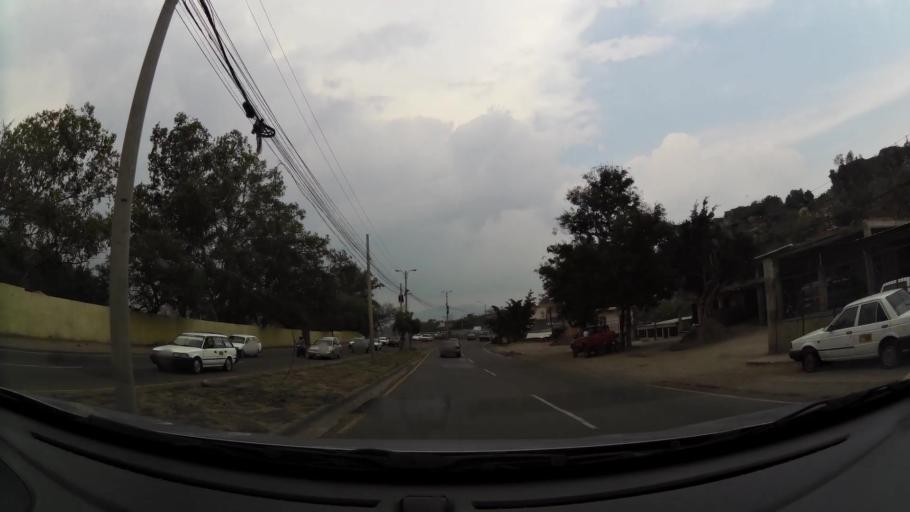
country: HN
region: Francisco Morazan
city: Tegucigalpa
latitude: 14.0850
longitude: -87.2206
